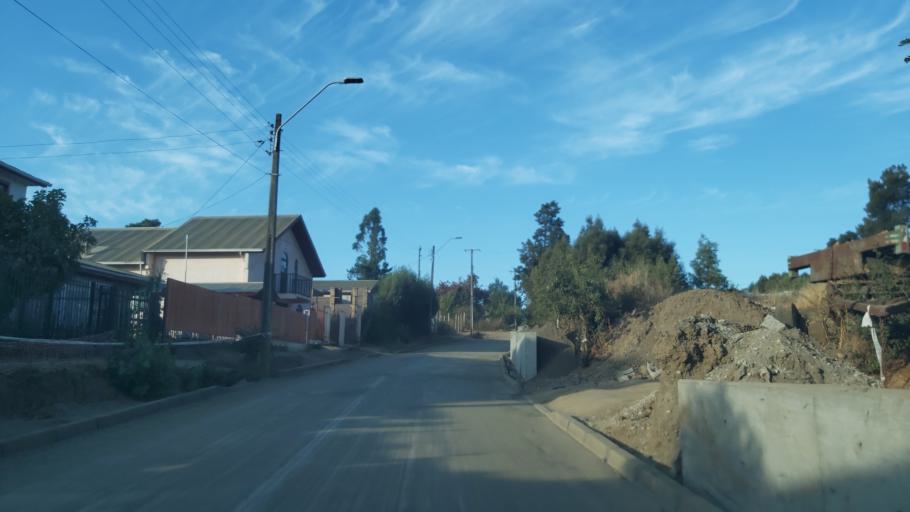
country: CL
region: Biobio
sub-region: Provincia de Biobio
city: La Laja
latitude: -37.1609
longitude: -72.9115
